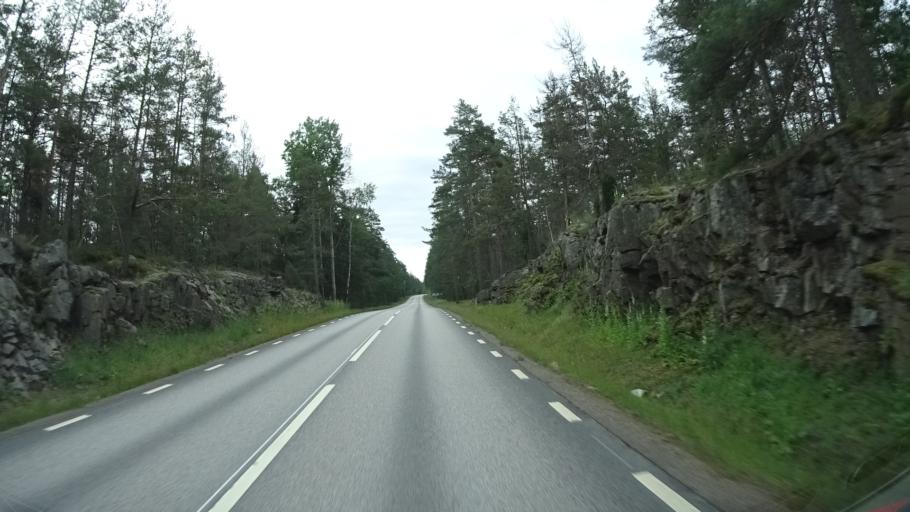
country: SE
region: Kalmar
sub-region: Oskarshamns Kommun
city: Oskarshamn
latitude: 57.2677
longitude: 16.3121
